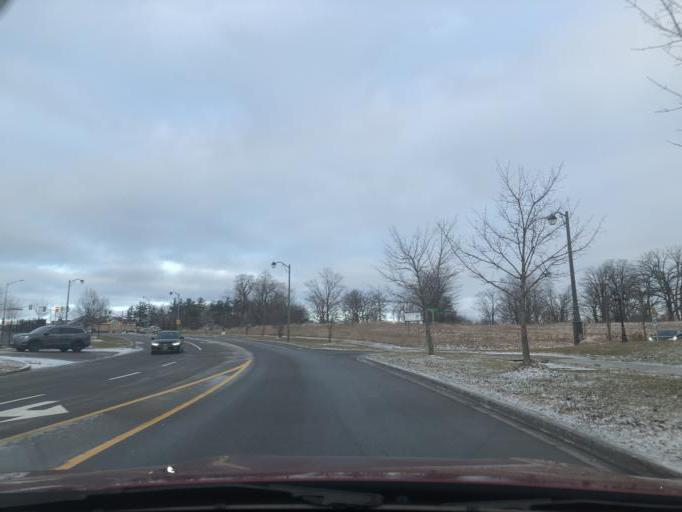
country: CA
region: Ontario
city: Markham
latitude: 43.8640
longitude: -79.2305
